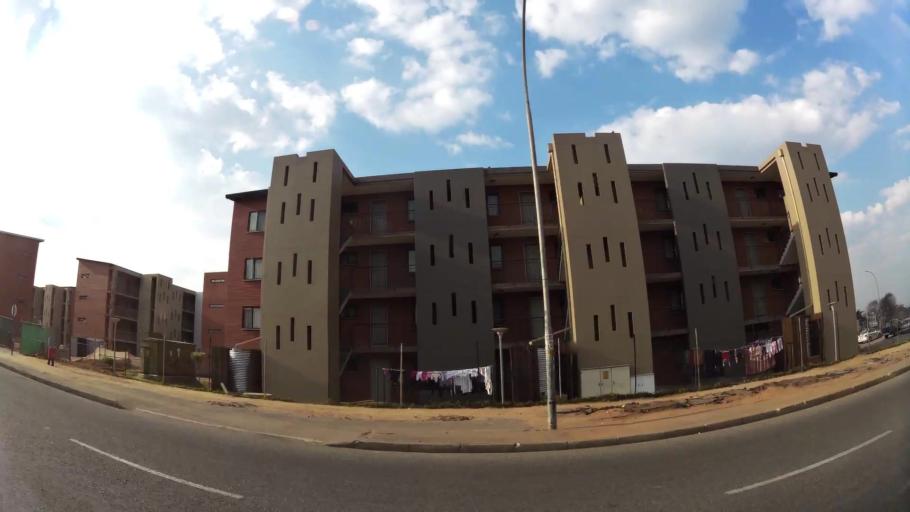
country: ZA
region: Gauteng
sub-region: Ekurhuleni Metropolitan Municipality
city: Germiston
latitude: -26.2211
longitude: 28.1698
